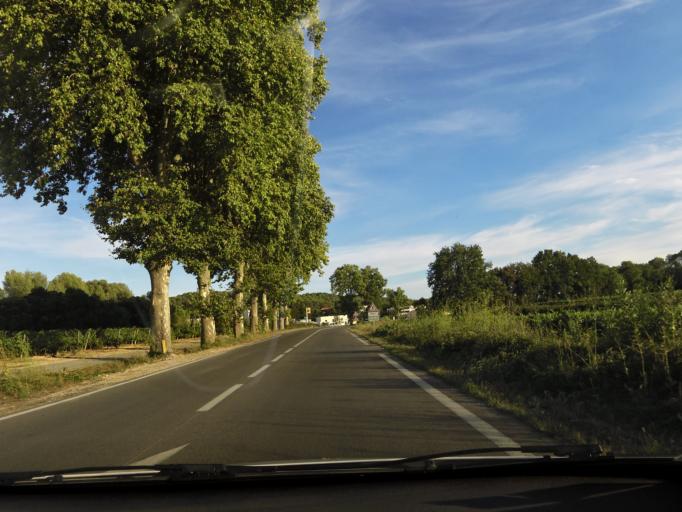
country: FR
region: Languedoc-Roussillon
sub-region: Departement de l'Herault
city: Montferrier-sur-Lez
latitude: 43.6788
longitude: 3.8665
